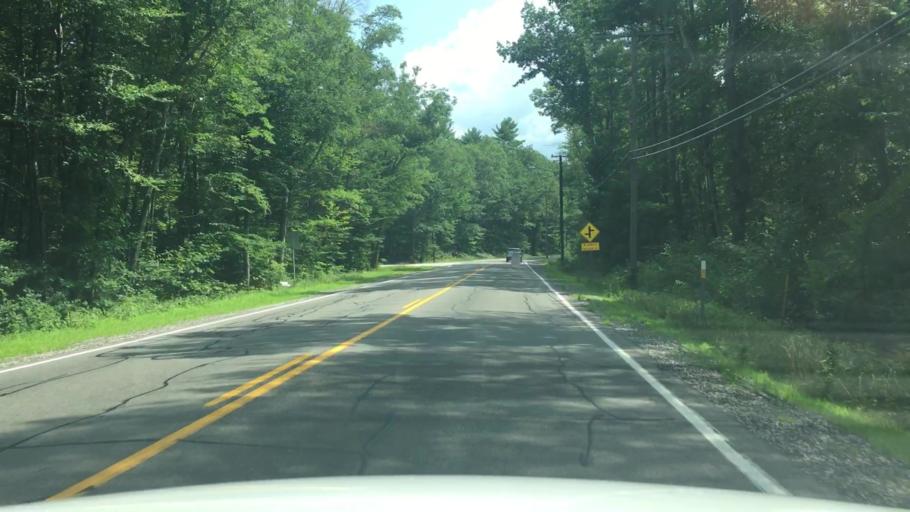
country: US
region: New Hampshire
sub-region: Rockingham County
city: Auburn
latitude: 42.9816
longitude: -71.3708
